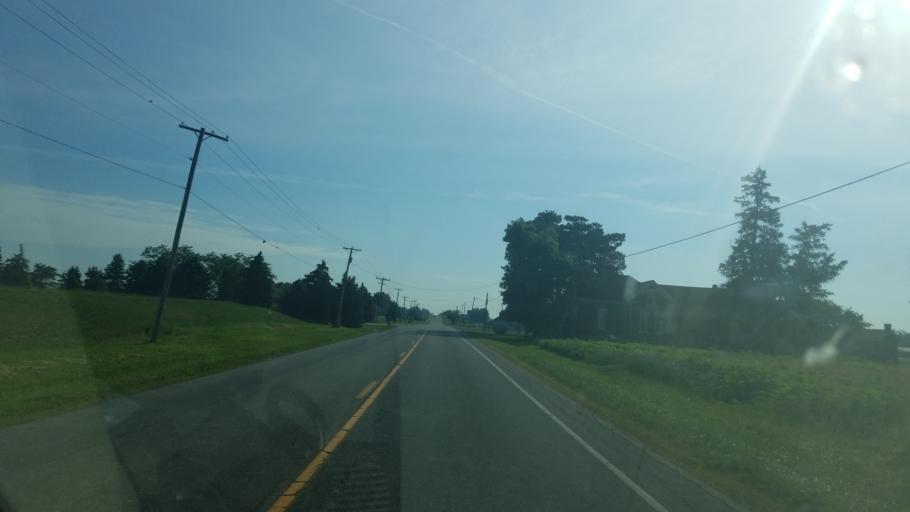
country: US
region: Ohio
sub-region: Hancock County
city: Findlay
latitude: 41.0068
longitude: -83.6934
